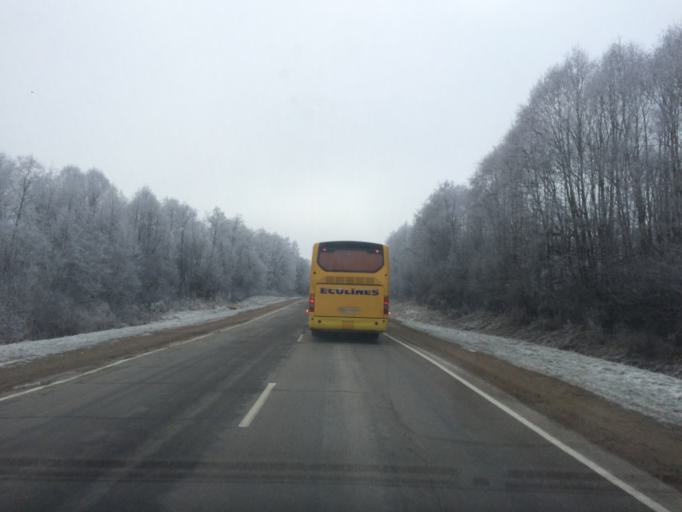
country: LV
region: Rezekne
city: Rezekne
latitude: 56.5536
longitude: 27.3595
